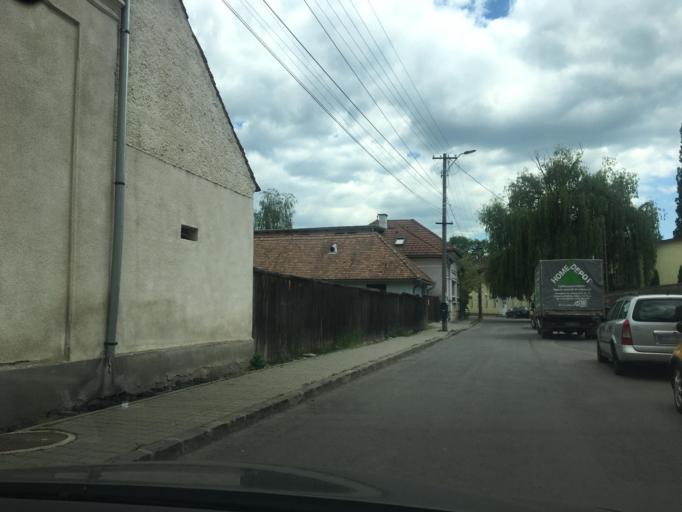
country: RO
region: Harghita
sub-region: Municipiul Gheorgheni
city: Gheorgheni
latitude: 46.7223
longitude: 25.6043
